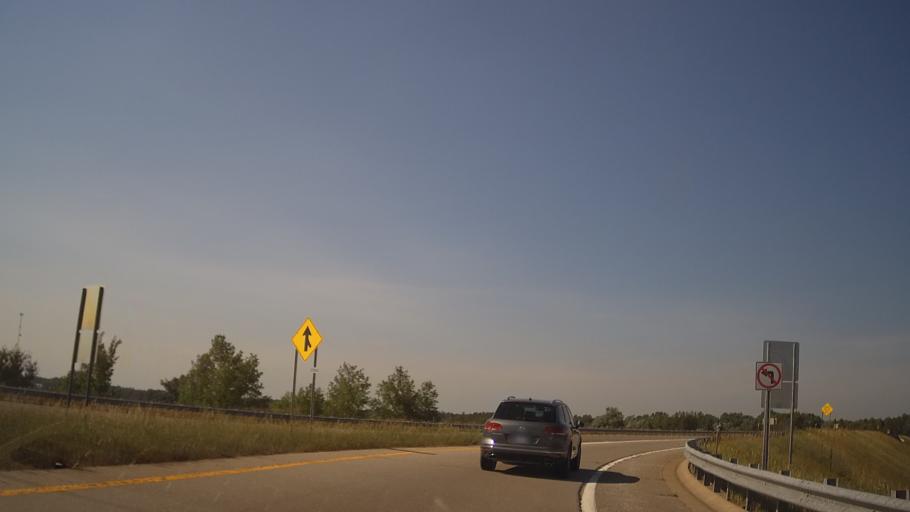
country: US
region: Michigan
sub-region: Ogemaw County
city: Skidway Lake
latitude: 44.1331
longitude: -84.1299
